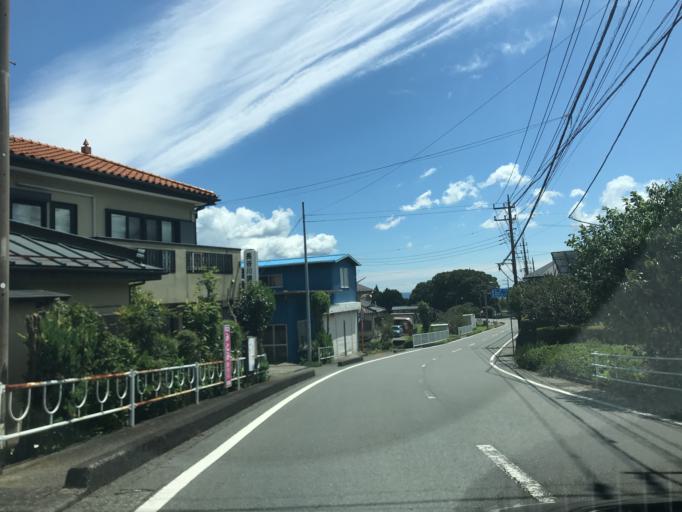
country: JP
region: Shizuoka
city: Gotemba
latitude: 35.2503
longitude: 138.8481
